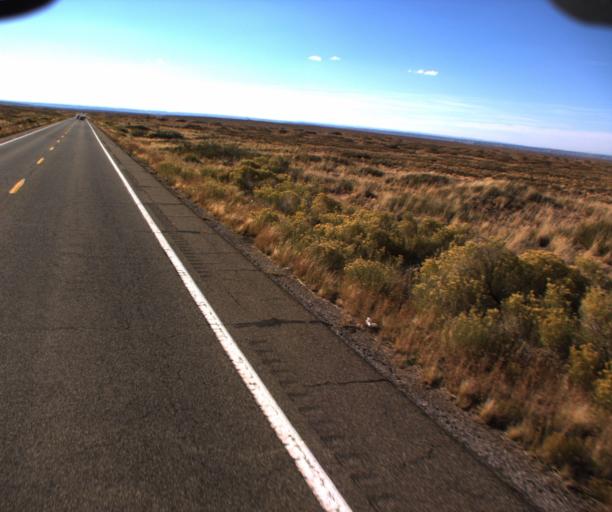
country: US
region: Arizona
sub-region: Coconino County
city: Kaibito
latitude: 36.6133
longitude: -111.0050
